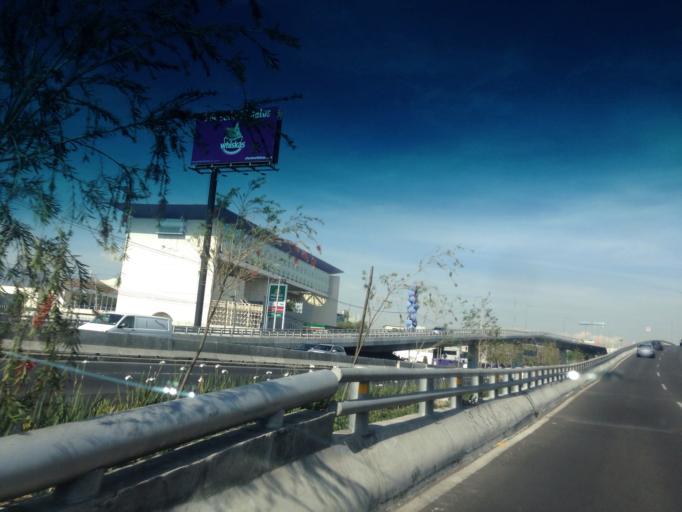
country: MX
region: Mexico City
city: Tlalpan
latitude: 19.2860
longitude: -99.1479
